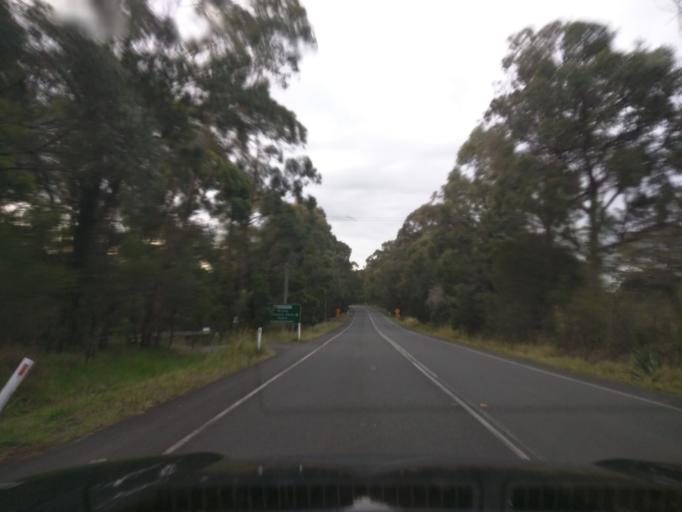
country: AU
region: New South Wales
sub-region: Wollondilly
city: Douglas Park
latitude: -34.2416
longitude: 150.7279
